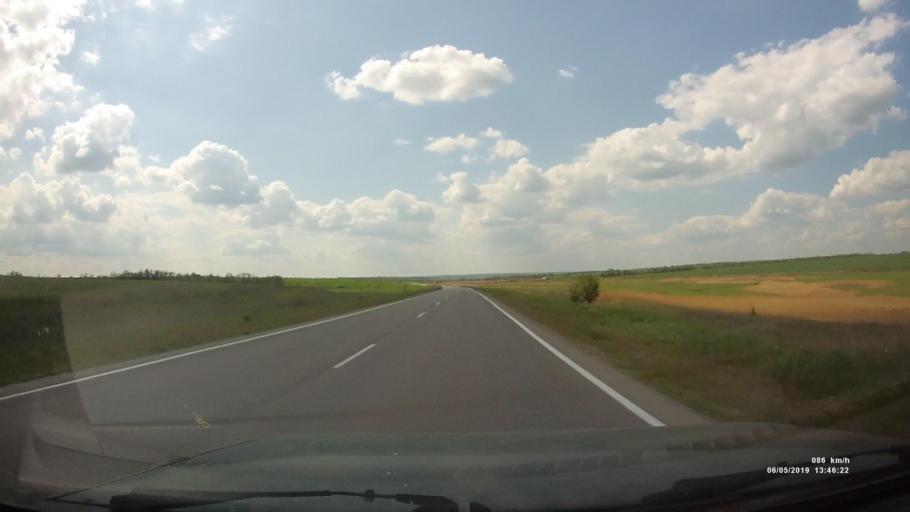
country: RU
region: Rostov
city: Melikhovskaya
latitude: 47.6585
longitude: 40.5809
